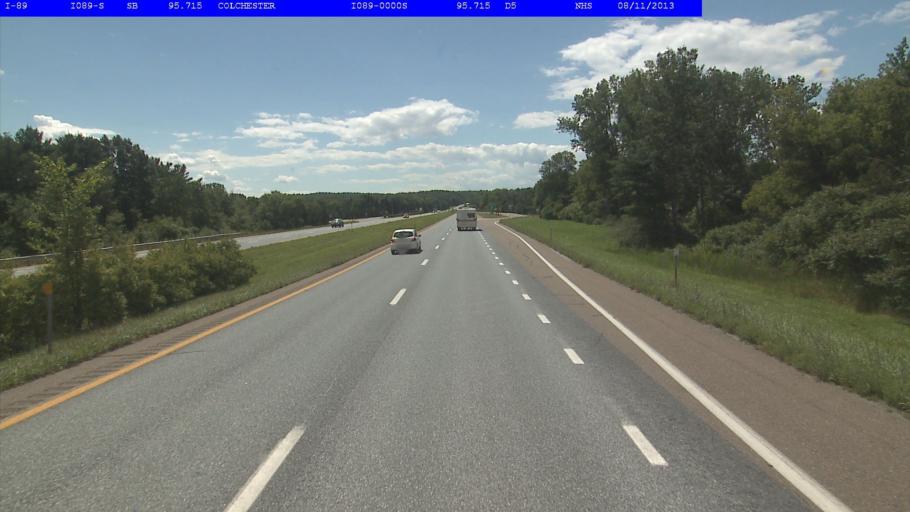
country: US
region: Vermont
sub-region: Chittenden County
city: Colchester
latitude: 44.5598
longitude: -73.1813
